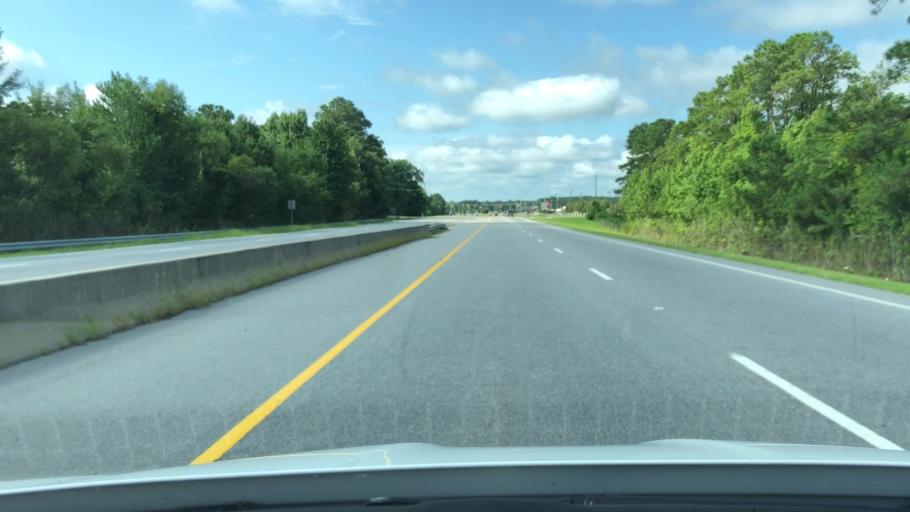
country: US
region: North Carolina
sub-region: Perquimans County
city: Hertford
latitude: 36.1828
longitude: -76.4594
